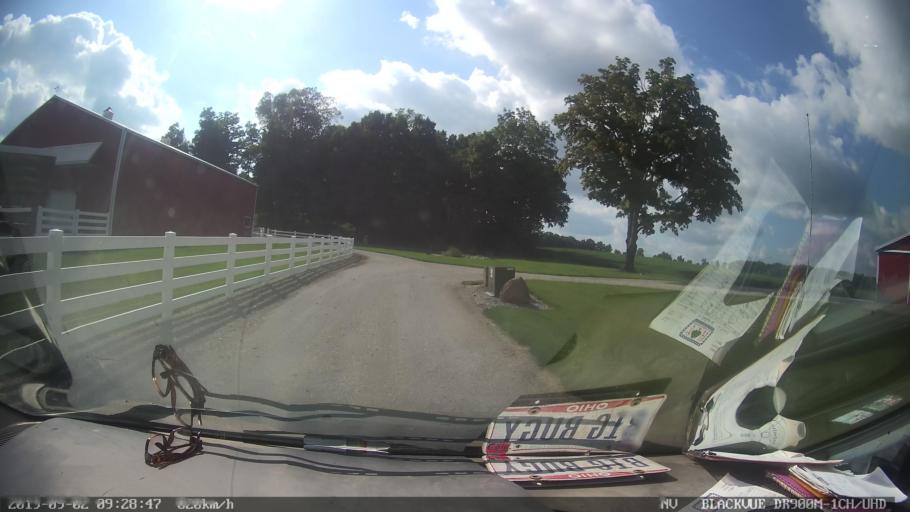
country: US
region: Ohio
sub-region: Knox County
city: Centerburg
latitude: 40.4143
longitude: -82.7059
